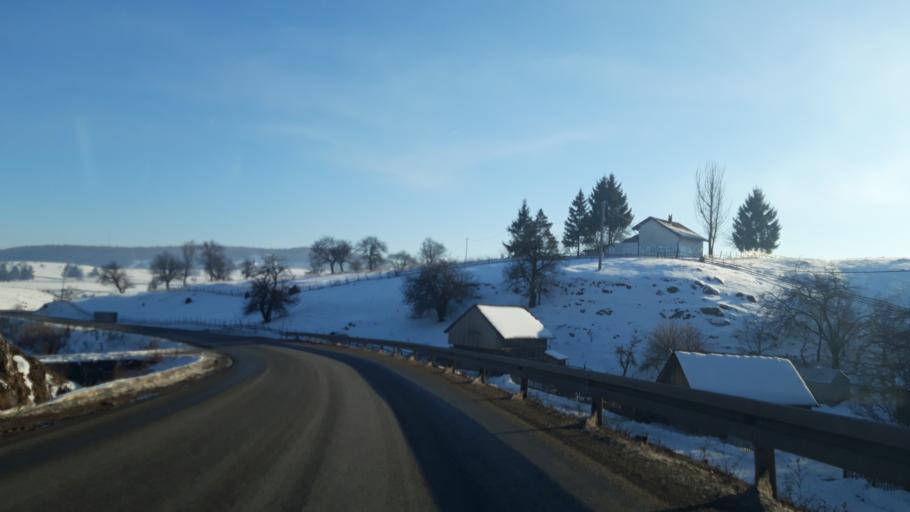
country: BA
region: Republika Srpska
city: Sokolac
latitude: 43.9204
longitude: 18.7573
